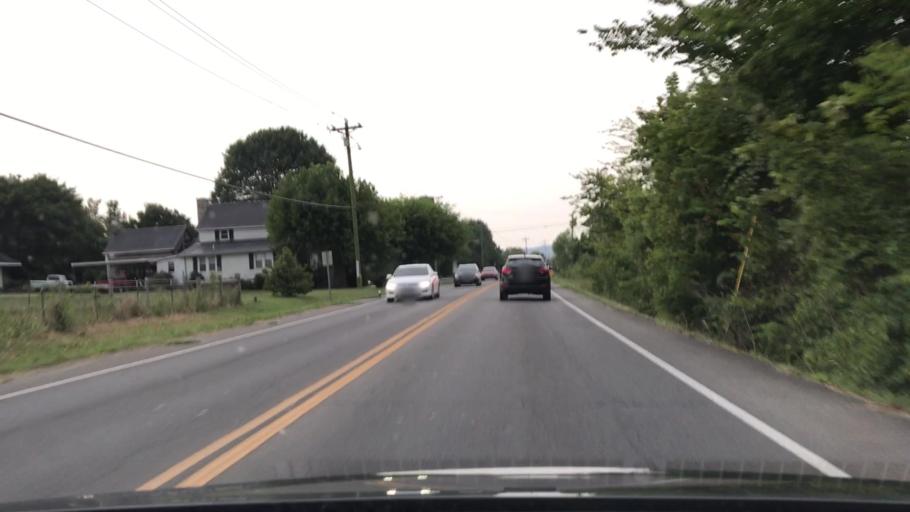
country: US
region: Tennessee
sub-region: Williamson County
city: Nolensville
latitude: 35.9782
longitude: -86.6782
